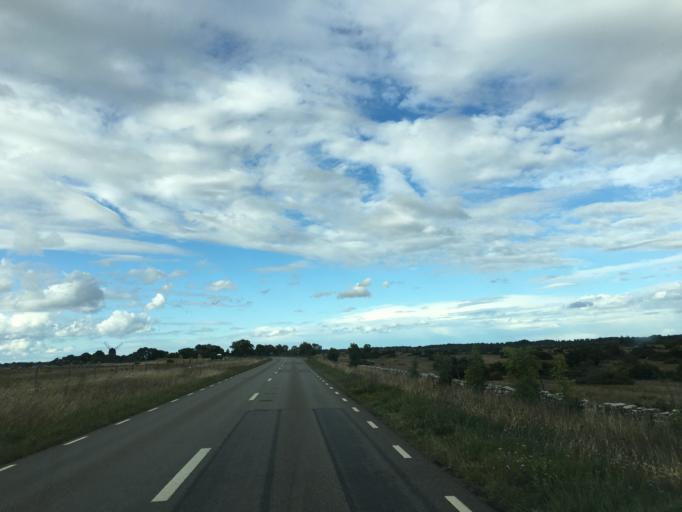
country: SE
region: Kalmar
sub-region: Morbylanga Kommun
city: Moerbylanga
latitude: 56.3853
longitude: 16.4333
